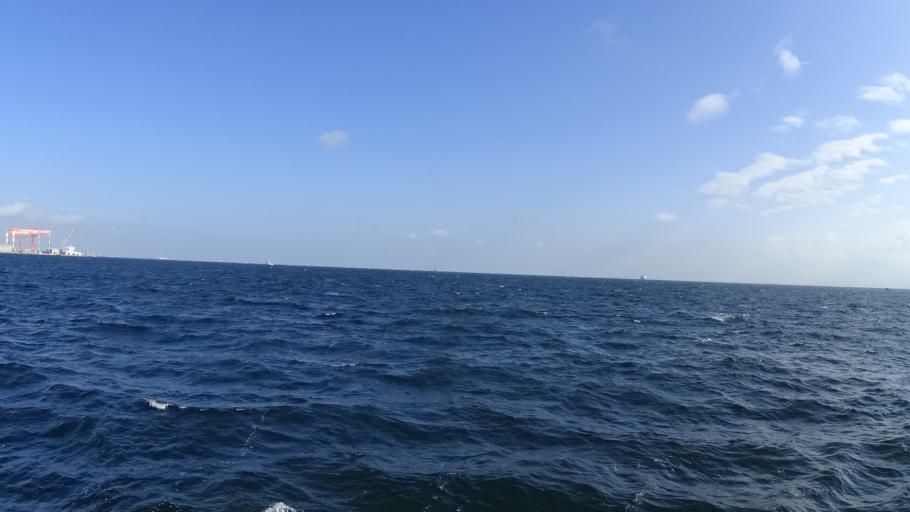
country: JP
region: Kanagawa
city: Yokosuka
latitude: 35.3064
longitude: 139.6568
